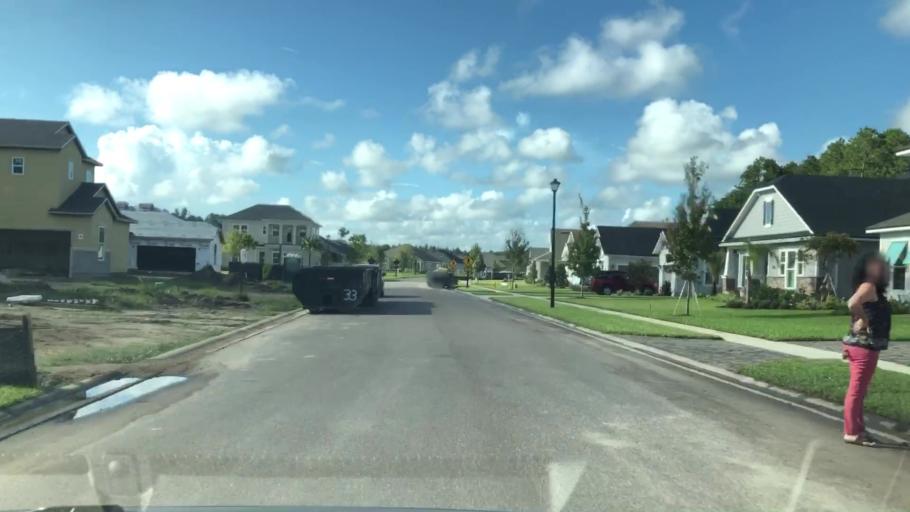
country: US
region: Florida
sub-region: Saint Johns County
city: Palm Valley
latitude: 30.1397
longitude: -81.4133
